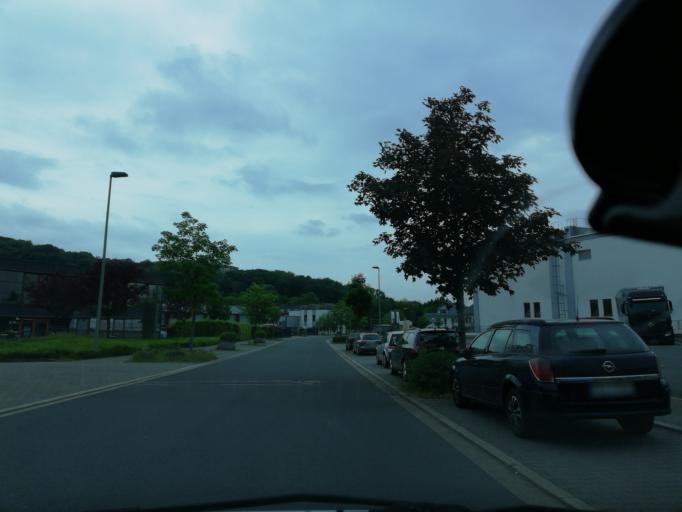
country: DE
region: North Rhine-Westphalia
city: Wetter (Ruhr)
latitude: 51.3814
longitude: 7.3883
